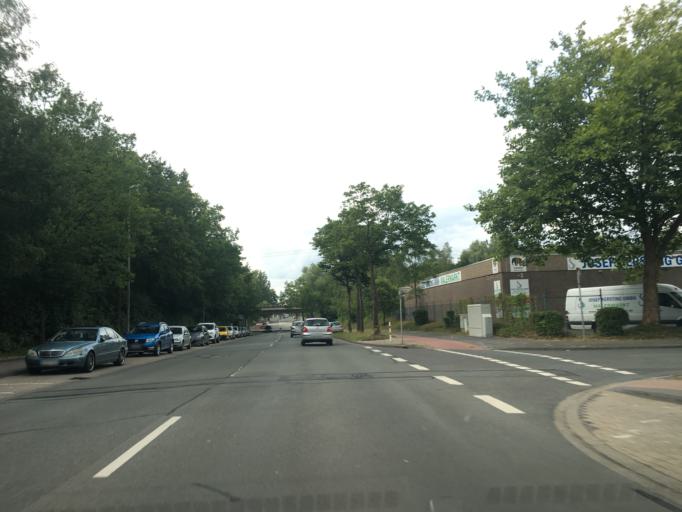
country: DE
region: North Rhine-Westphalia
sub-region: Regierungsbezirk Munster
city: Muenster
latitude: 51.9251
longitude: 7.6503
